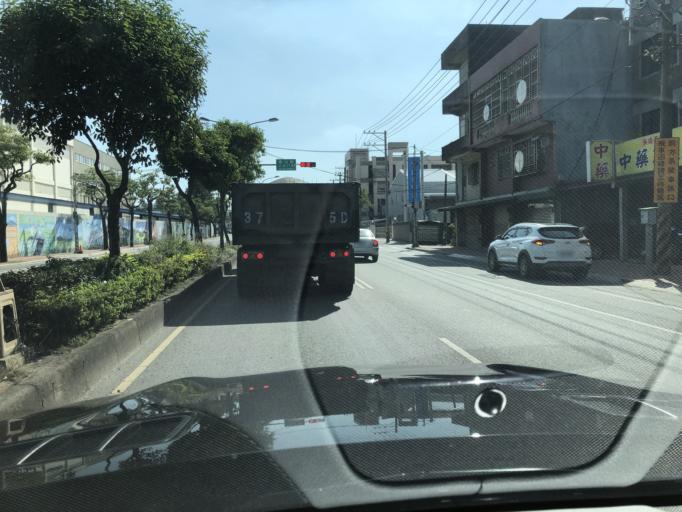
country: TW
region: Taiwan
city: Taoyuan City
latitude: 25.0774
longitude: 121.2854
